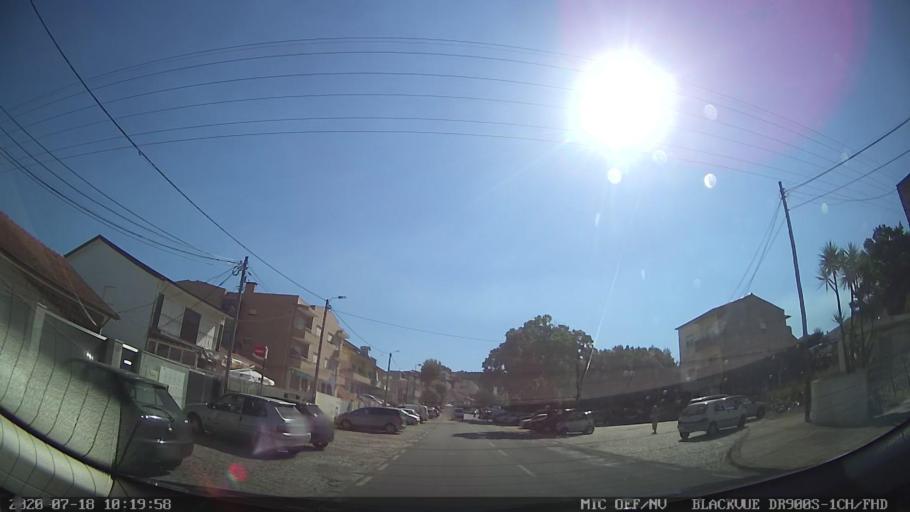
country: PT
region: Porto
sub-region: Valongo
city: Valongo
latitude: 41.1911
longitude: -8.5215
